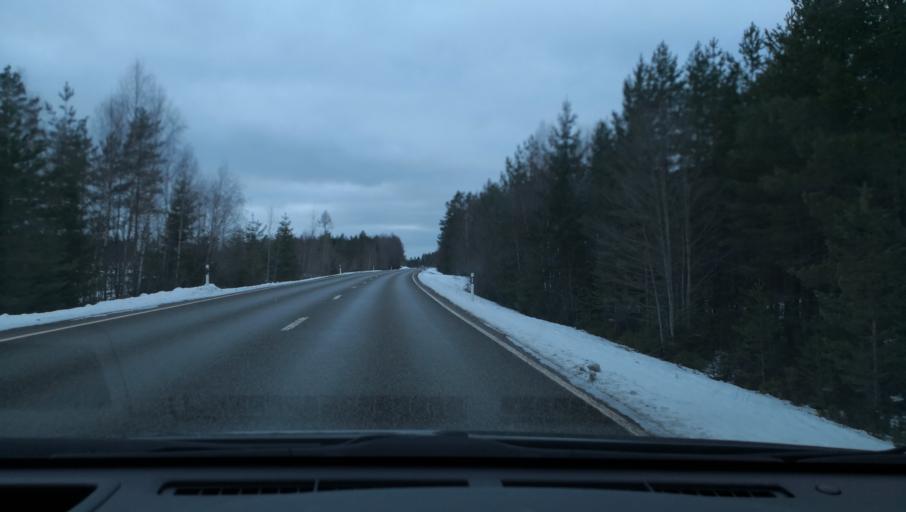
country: SE
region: Vaestmanland
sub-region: Surahammars Kommun
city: Ramnas
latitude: 59.7844
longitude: 16.0256
